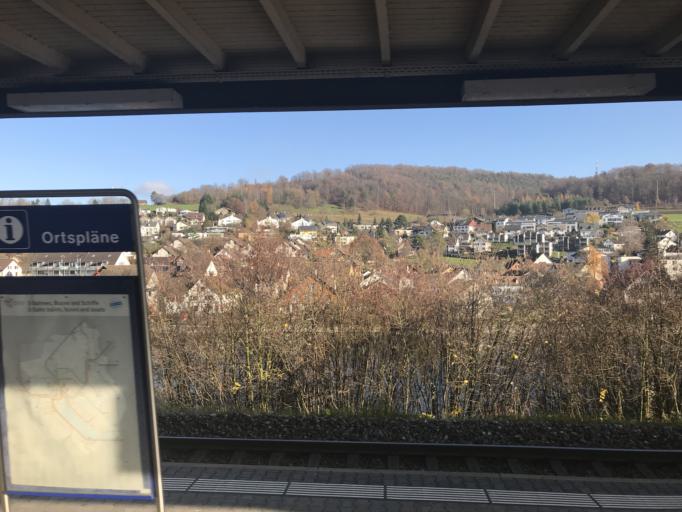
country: CH
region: Zurich
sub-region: Bezirk Andelfingen
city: Flurlingen
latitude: 47.6831
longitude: 8.6253
